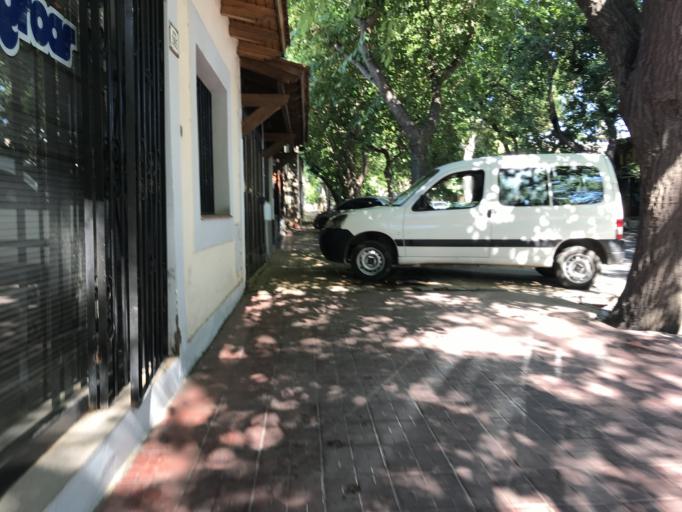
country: AR
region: Mendoza
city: Mendoza
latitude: -32.8766
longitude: -68.8309
